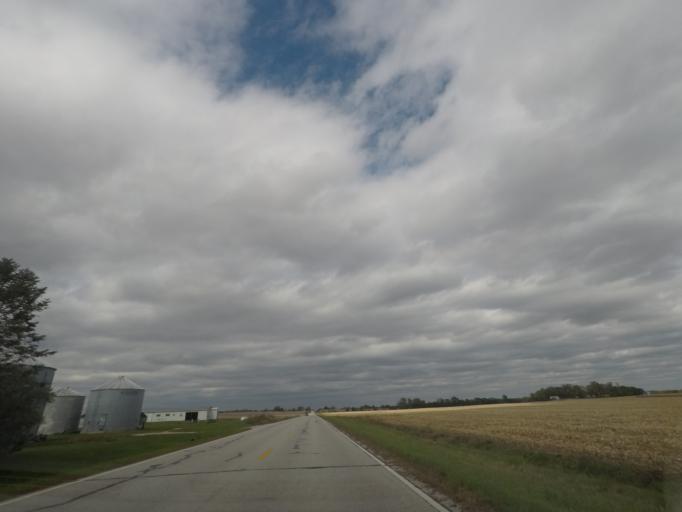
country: US
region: Iowa
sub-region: Story County
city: Huxley
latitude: 41.8498
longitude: -93.5315
